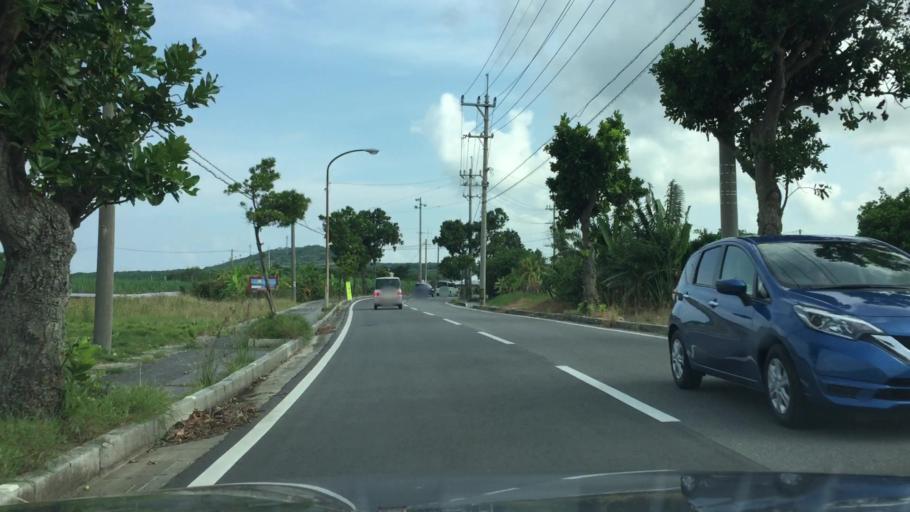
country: JP
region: Okinawa
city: Ishigaki
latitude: 24.4584
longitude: 124.2493
